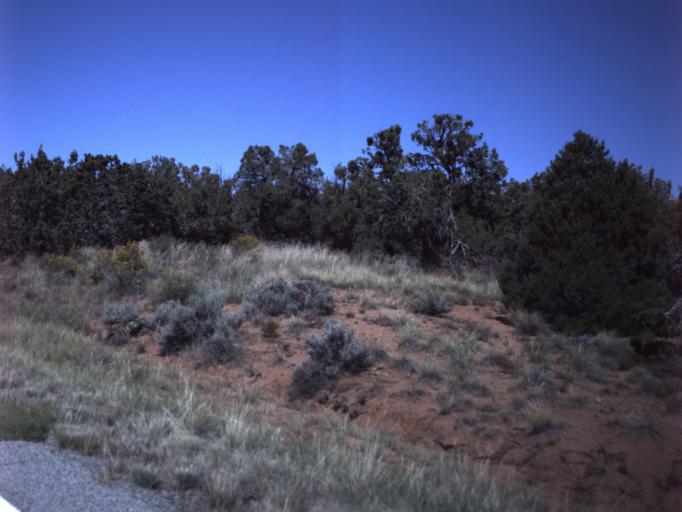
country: US
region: Utah
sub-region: San Juan County
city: Blanding
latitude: 37.5417
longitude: -109.7491
